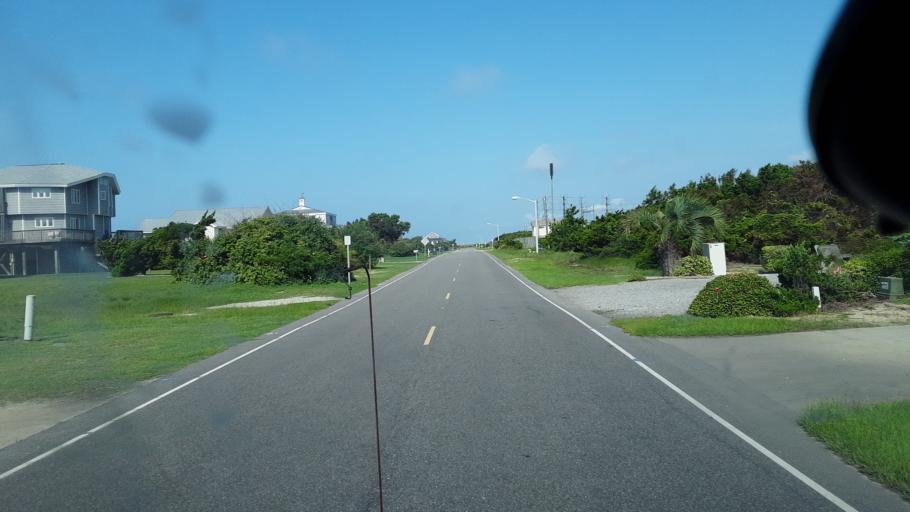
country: US
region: North Carolina
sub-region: Brunswick County
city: Southport
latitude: 33.8967
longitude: -78.0509
